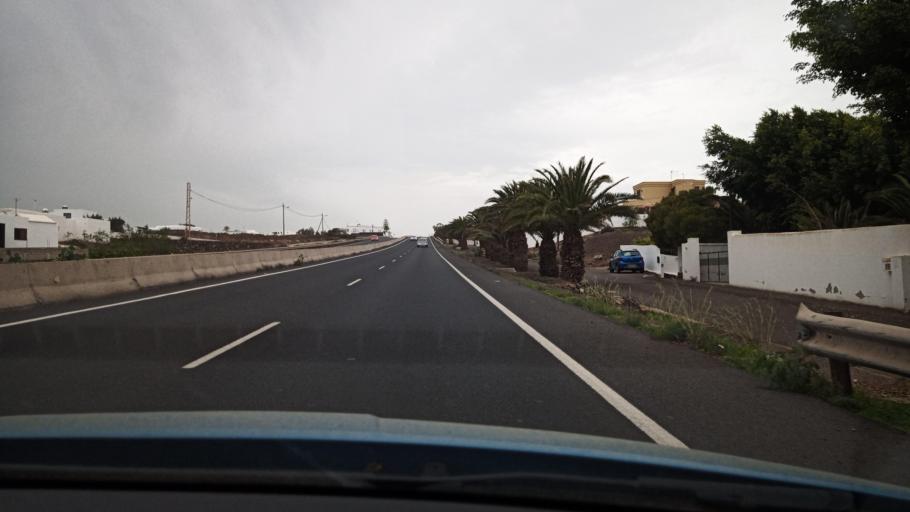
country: ES
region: Canary Islands
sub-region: Provincia de Las Palmas
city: Tias
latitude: 28.9570
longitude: -13.6399
